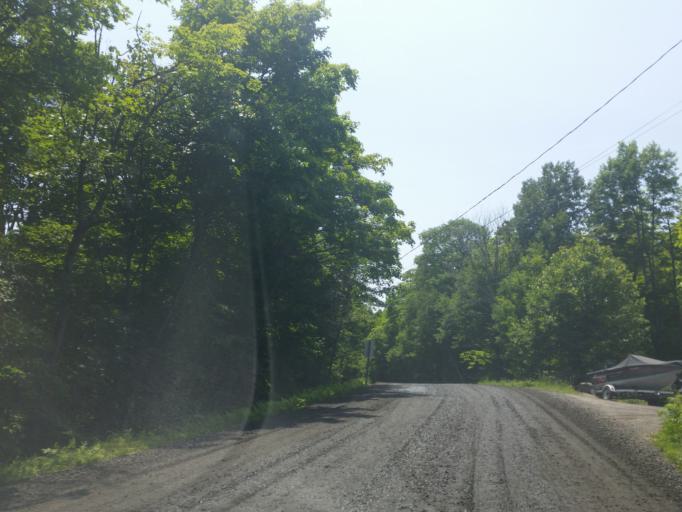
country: CA
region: Ontario
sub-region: Parry Sound District
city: Parry Sound
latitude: 45.4350
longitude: -80.0127
